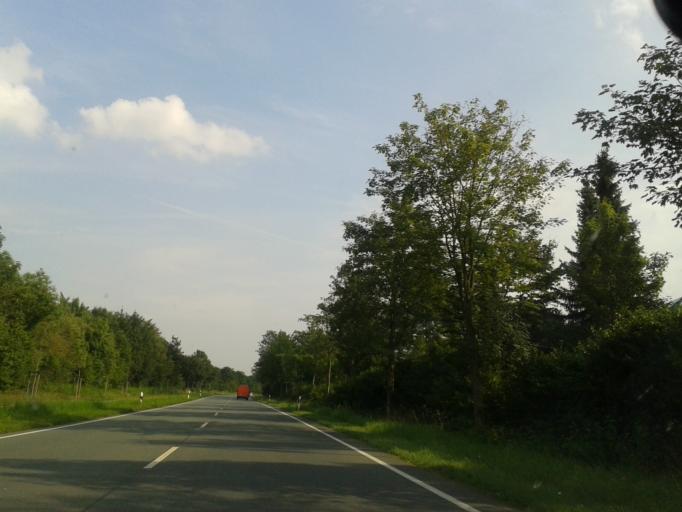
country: DE
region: North Rhine-Westphalia
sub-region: Regierungsbezirk Detmold
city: Paderborn
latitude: 51.7358
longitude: 8.7893
